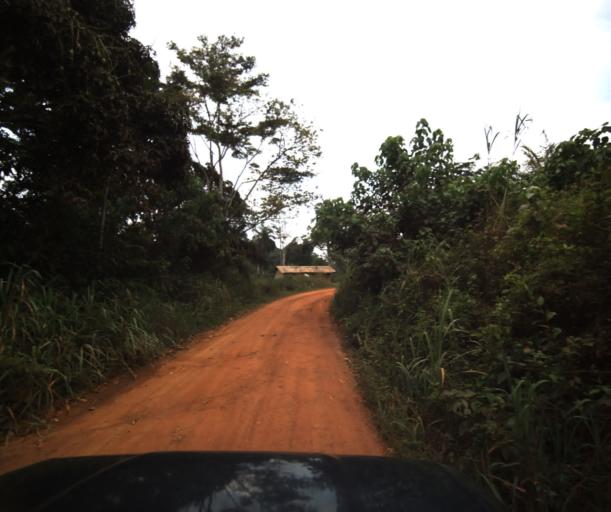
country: CM
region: Centre
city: Akono
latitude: 3.5953
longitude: 11.1676
